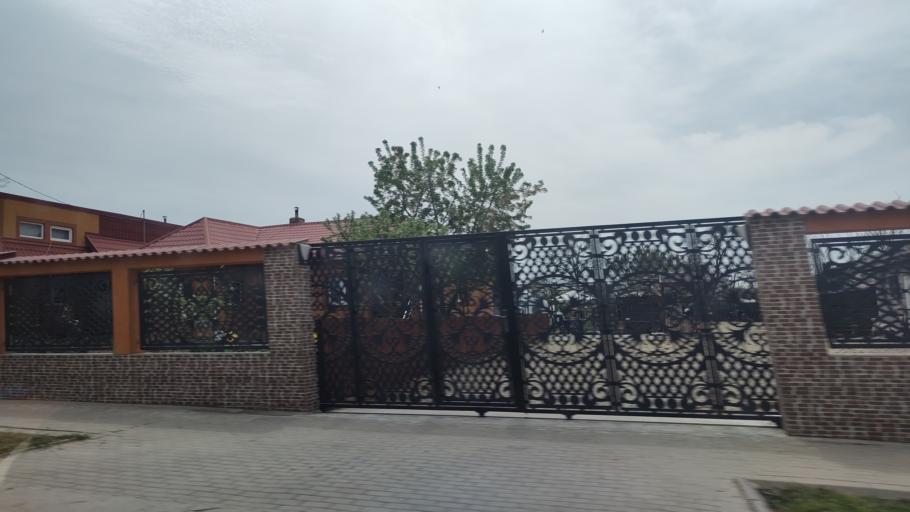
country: RO
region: Constanta
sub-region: Comuna Ciocarlia
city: Ciocarlia
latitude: 44.1047
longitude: 28.2899
